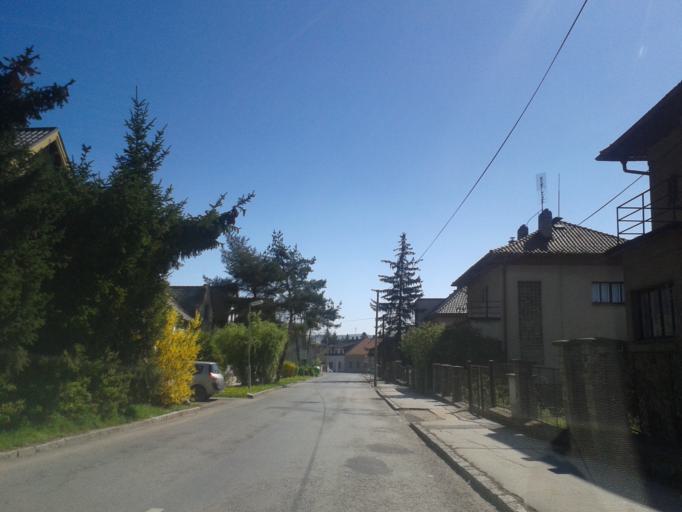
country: CZ
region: Central Bohemia
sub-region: Okres Beroun
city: Beroun
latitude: 49.9647
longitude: 14.0608
